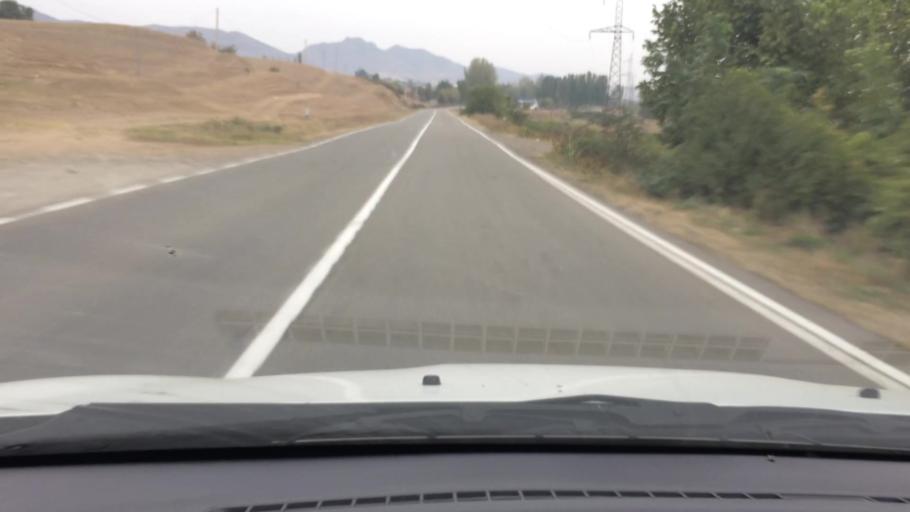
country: AM
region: Tavush
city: Bagratashen
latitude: 41.2875
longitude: 44.7893
